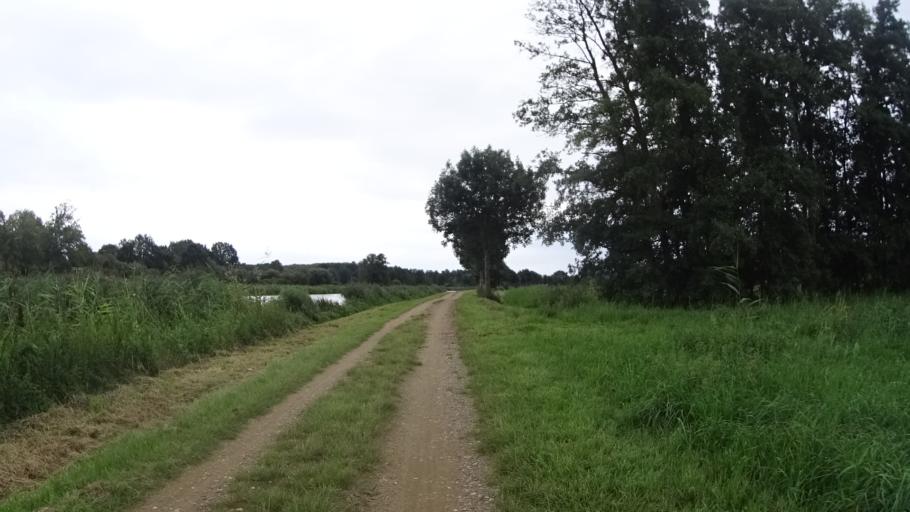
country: DE
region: Schleswig-Holstein
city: Kuhsen
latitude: 53.6817
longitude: 10.6350
